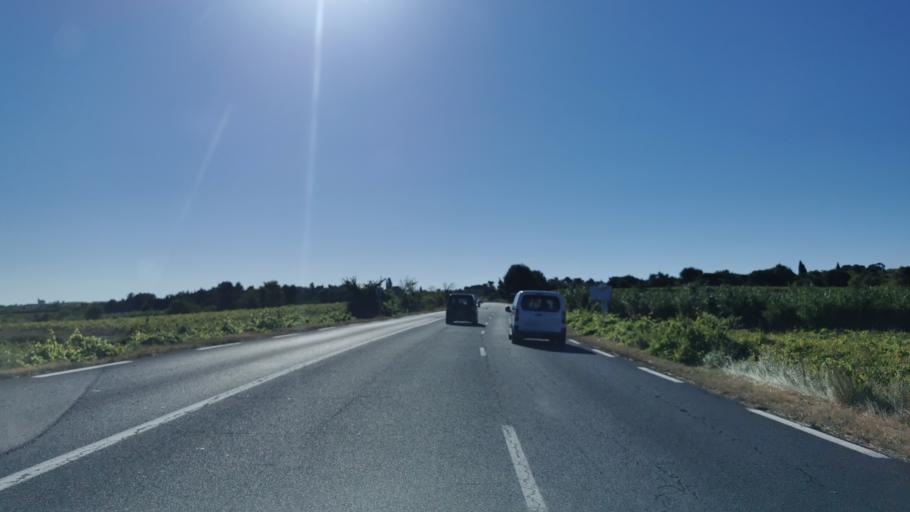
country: FR
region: Languedoc-Roussillon
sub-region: Departement de l'Herault
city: Nissan-lez-Enserune
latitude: 43.2953
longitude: 3.1362
